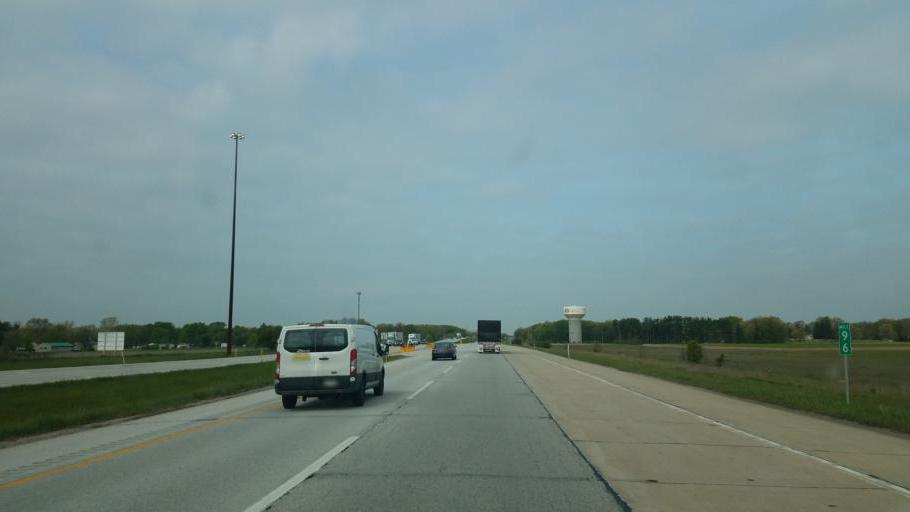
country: US
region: Indiana
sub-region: Elkhart County
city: Bristol
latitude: 41.7304
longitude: -85.8890
